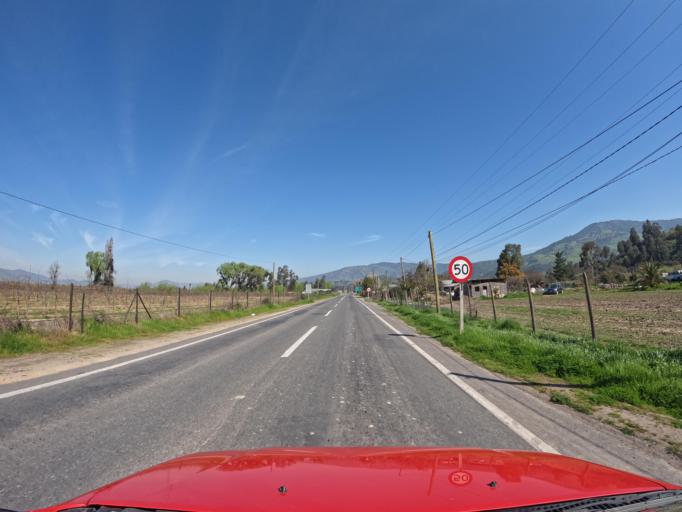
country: CL
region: Maule
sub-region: Provincia de Curico
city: Rauco
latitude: -34.9787
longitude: -71.3973
